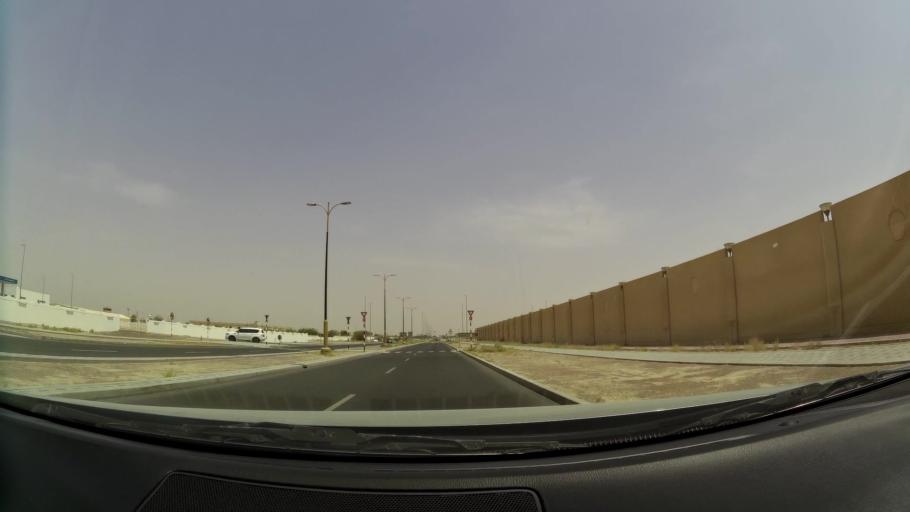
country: AE
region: Abu Dhabi
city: Al Ain
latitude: 24.1897
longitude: 55.7215
